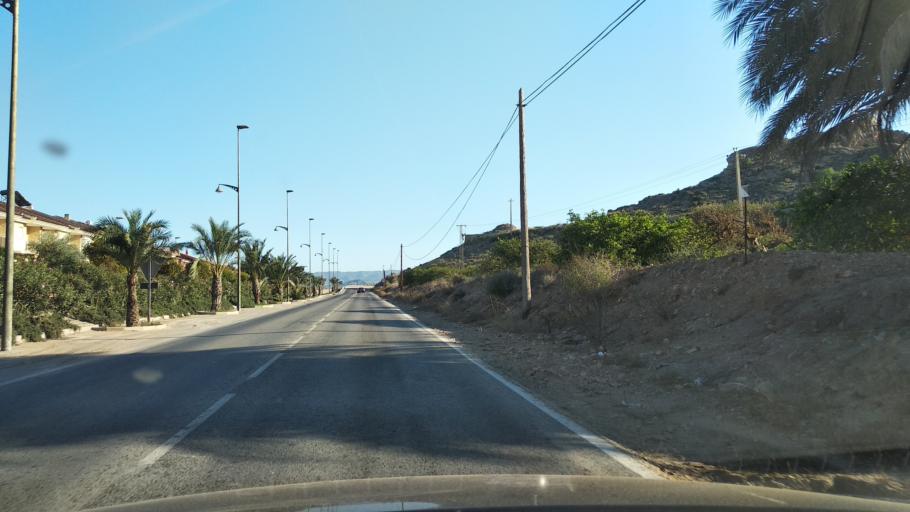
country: ES
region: Murcia
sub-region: Murcia
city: Santomera
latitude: 38.0583
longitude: -1.0535
